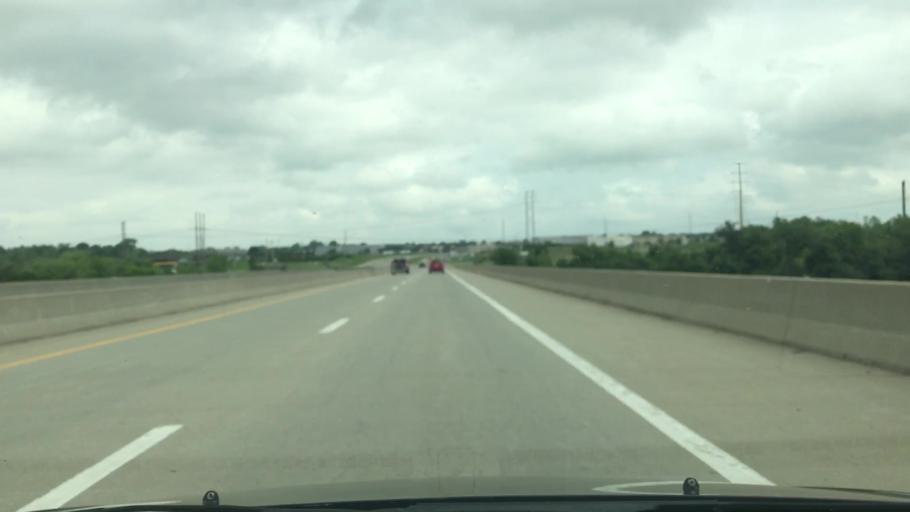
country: US
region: Missouri
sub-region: Jackson County
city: Grandview
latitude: 38.8702
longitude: -94.6017
